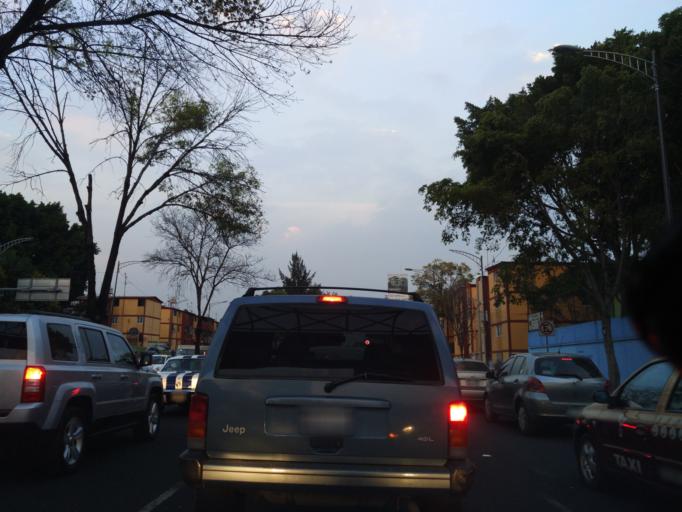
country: MX
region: Mexico City
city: Xochimilco
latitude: 19.3090
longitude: -99.1112
